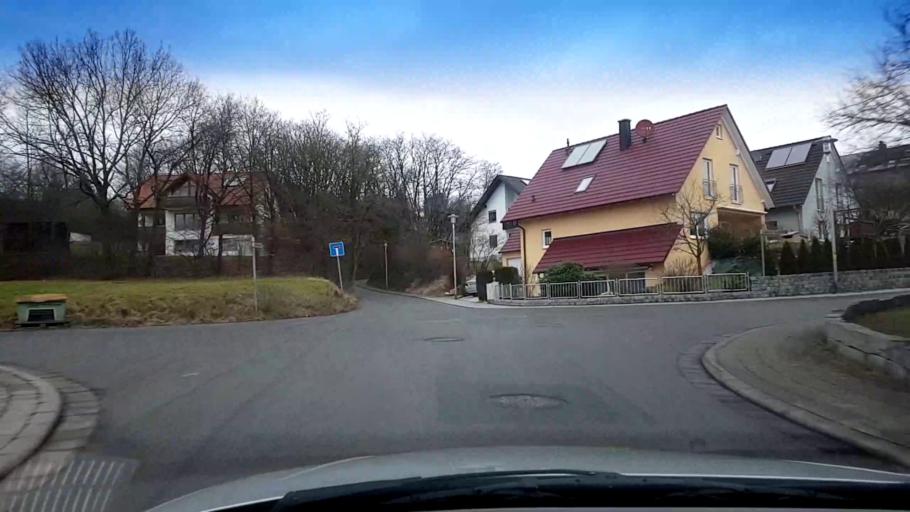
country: DE
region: Bavaria
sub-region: Upper Franconia
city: Hallstadt
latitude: 49.9324
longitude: 10.8564
